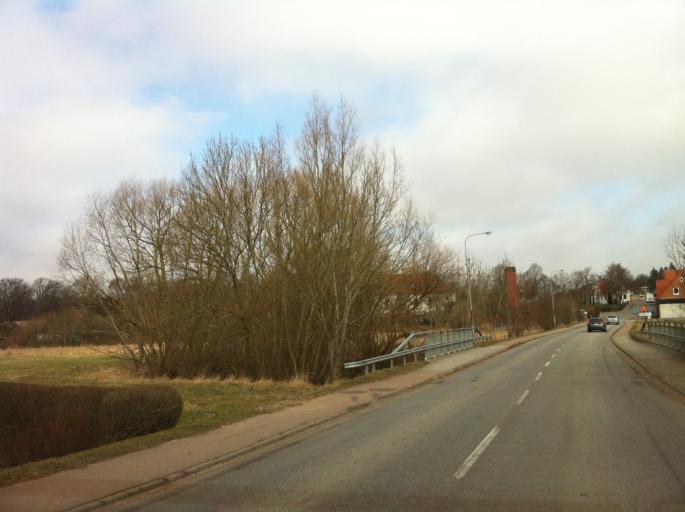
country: SE
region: Skane
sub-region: Svalovs Kommun
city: Teckomatorp
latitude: 55.8631
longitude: 13.0396
